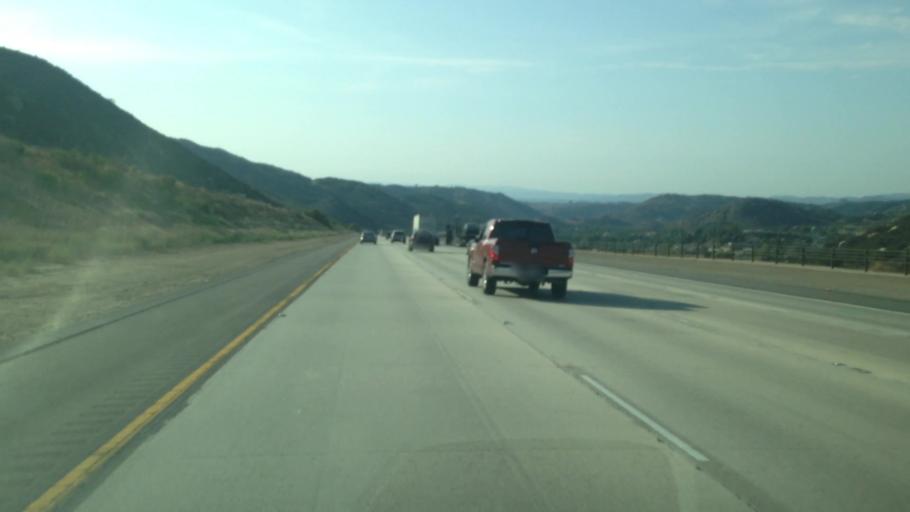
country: US
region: California
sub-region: San Diego County
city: Hidden Meadows
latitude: 33.2122
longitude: -117.1357
